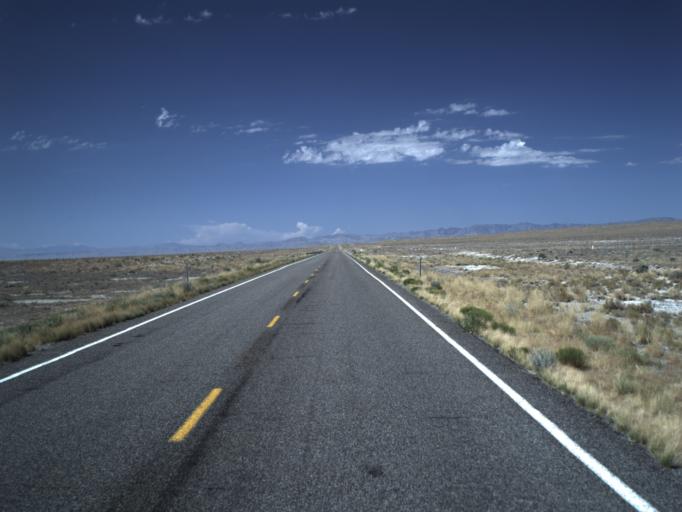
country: US
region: Utah
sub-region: Millard County
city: Delta
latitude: 39.1708
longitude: -113.0340
